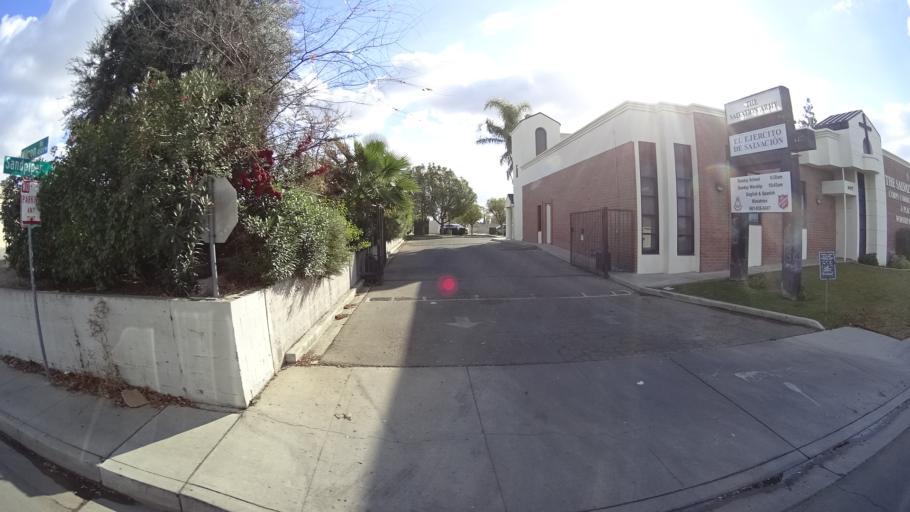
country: US
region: California
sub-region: Kern County
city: Bakersfield
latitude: 35.3323
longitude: -119.0540
